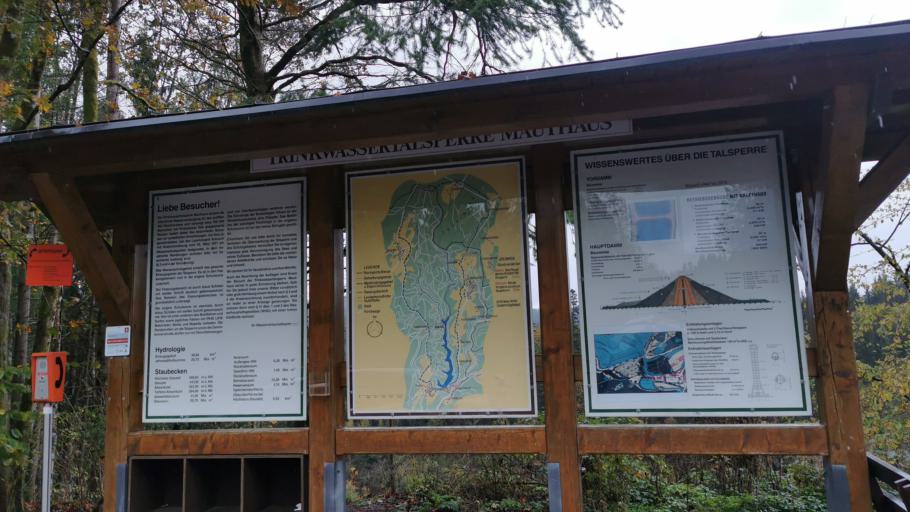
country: DE
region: Bavaria
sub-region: Upper Franconia
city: Steinwiesen
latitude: 50.3238
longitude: 11.4878
